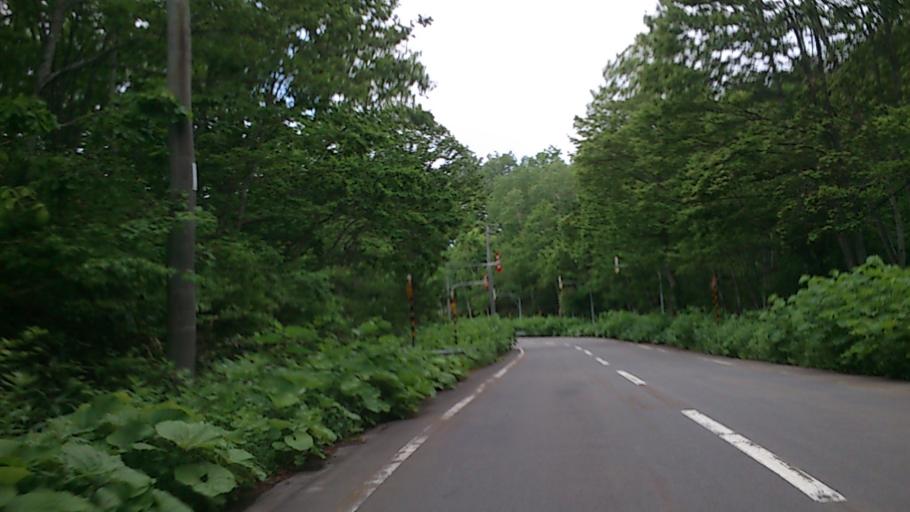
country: JP
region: Hokkaido
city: Iwanai
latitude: 42.8580
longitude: 140.5556
